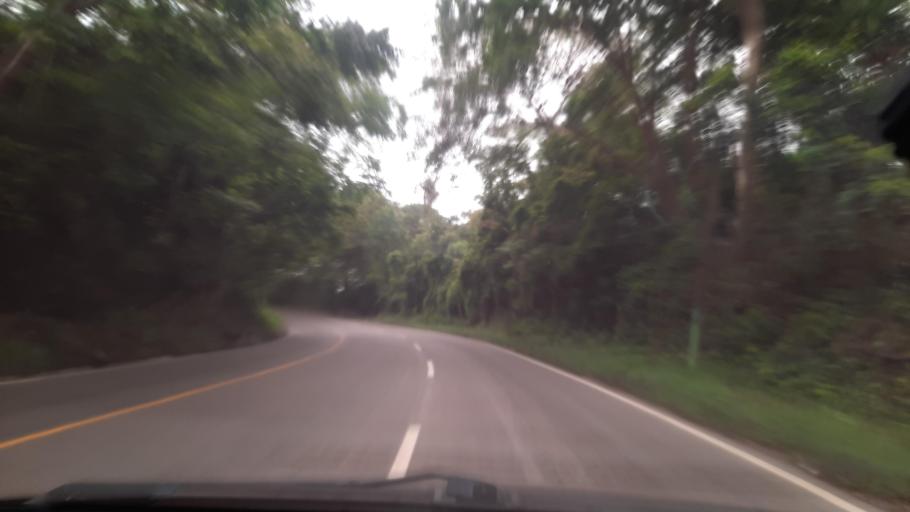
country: GT
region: Izabal
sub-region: Municipio de Los Amates
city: Los Amates
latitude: 15.2539
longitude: -89.1133
